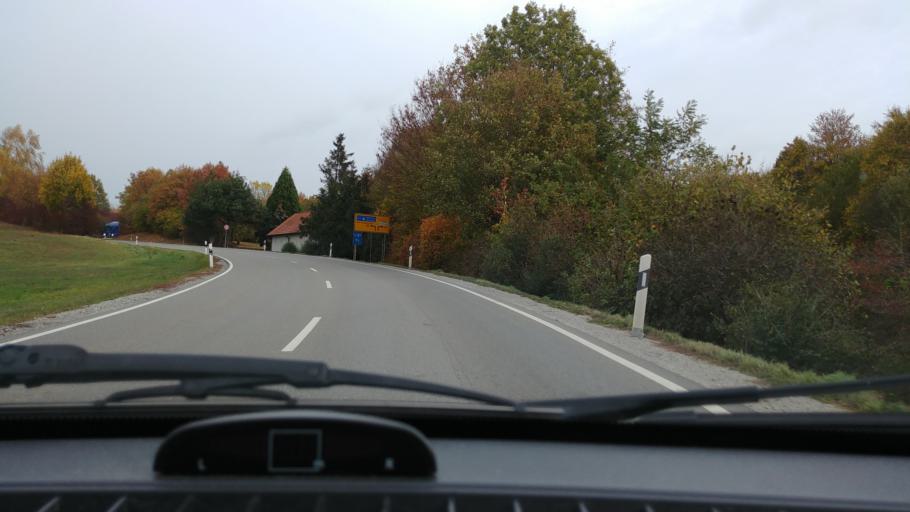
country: DE
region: Baden-Wuerttemberg
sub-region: Regierungsbezirk Stuttgart
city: Crailsheim
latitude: 49.1522
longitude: 10.0741
